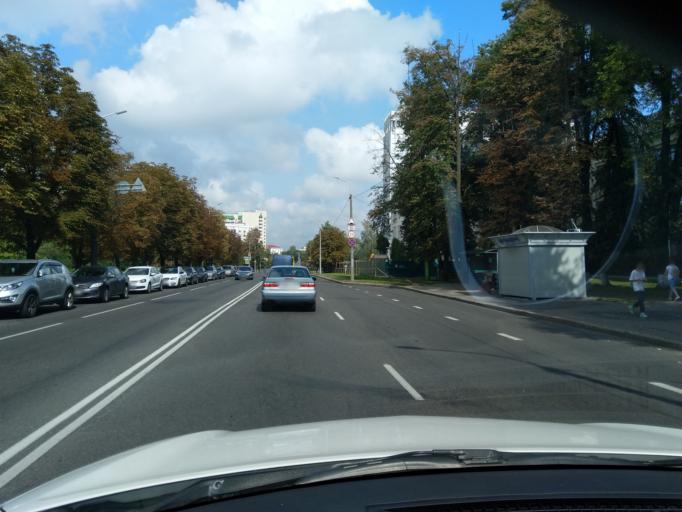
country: BY
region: Minsk
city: Minsk
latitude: 53.8988
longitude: 27.5863
